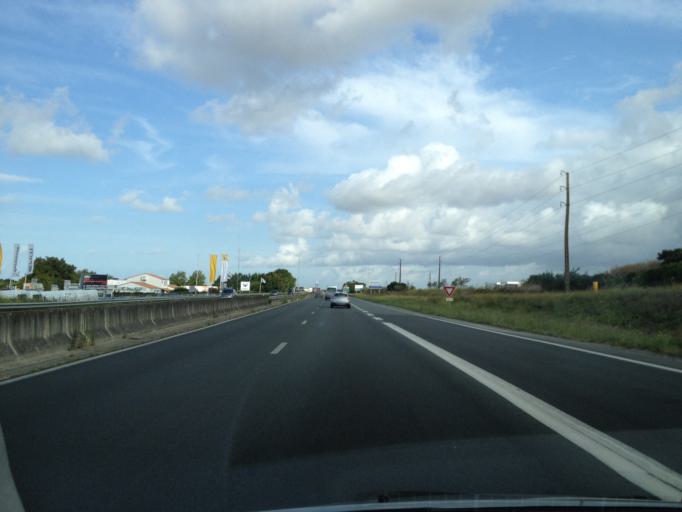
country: FR
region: Poitou-Charentes
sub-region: Departement de la Charente-Maritime
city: Perigny
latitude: 46.1559
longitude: -1.1160
